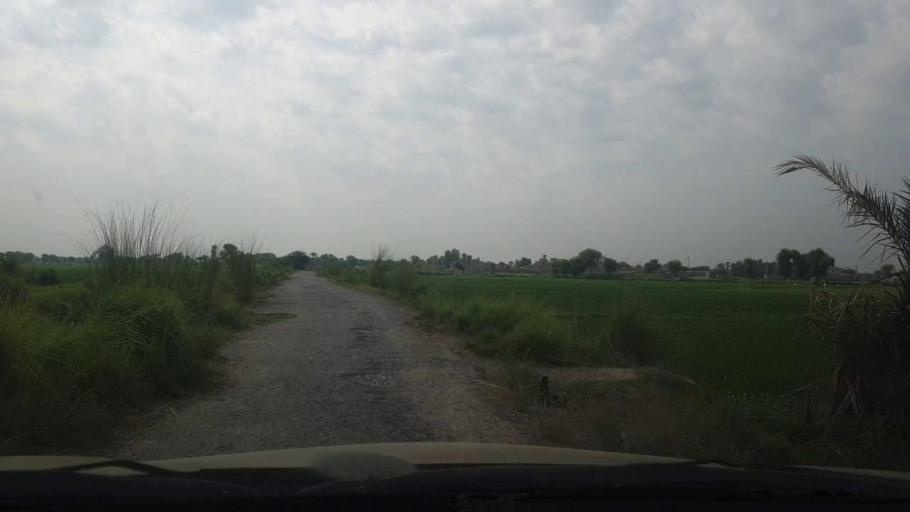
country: PK
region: Sindh
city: Larkana
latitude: 27.6409
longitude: 68.2032
